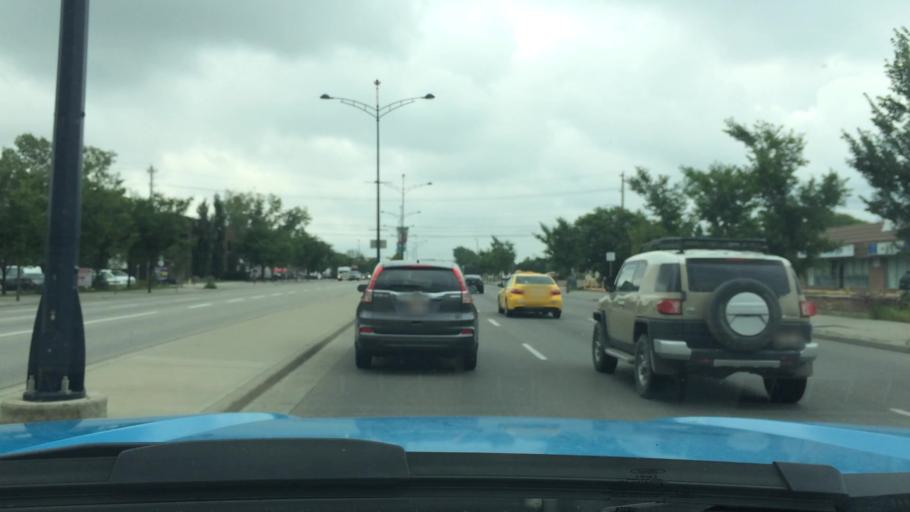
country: CA
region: Alberta
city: Calgary
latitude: 51.0668
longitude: -114.0547
